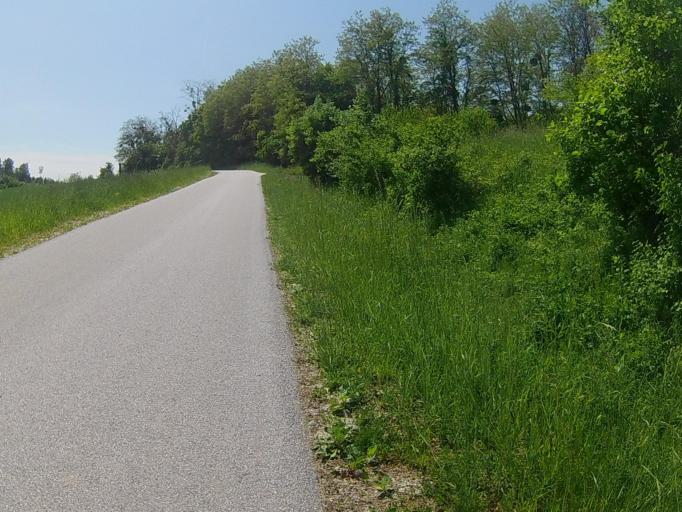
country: SI
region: Pesnica
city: Pesnica pri Mariboru
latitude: 46.5856
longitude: 15.6850
